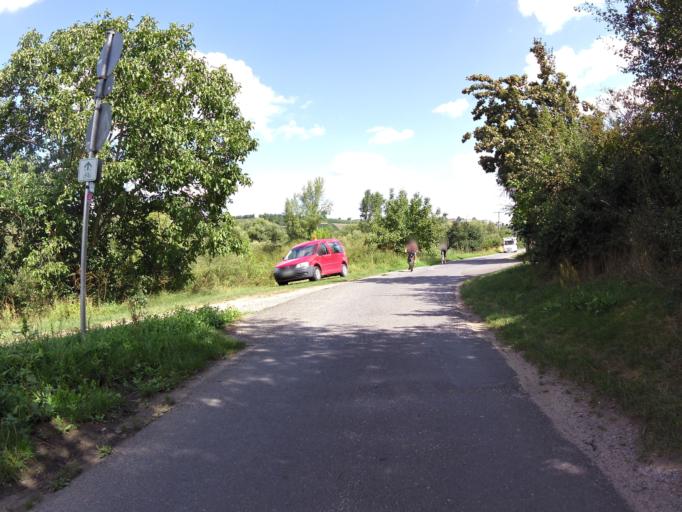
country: DE
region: Bavaria
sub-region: Regierungsbezirk Unterfranken
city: Nordheim
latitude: 49.8547
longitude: 10.1743
